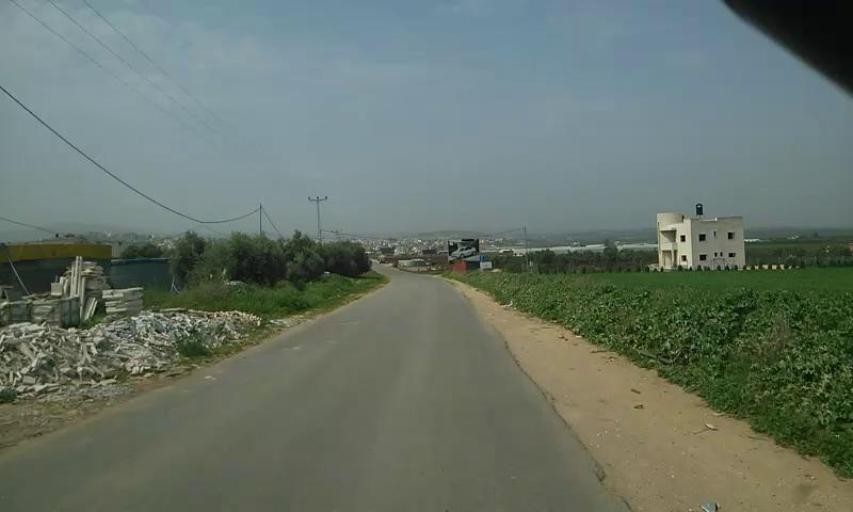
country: PS
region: West Bank
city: Kafr Dan
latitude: 32.4987
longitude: 35.2504
